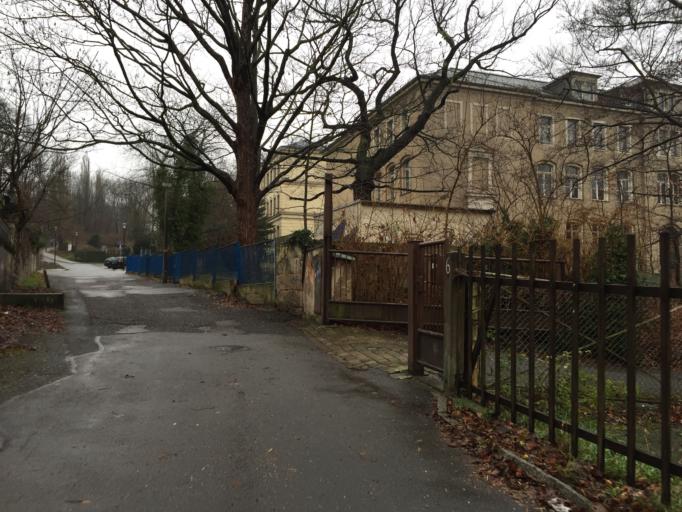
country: DE
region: Saxony
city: Bannewitz
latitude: 51.0289
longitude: 13.7038
